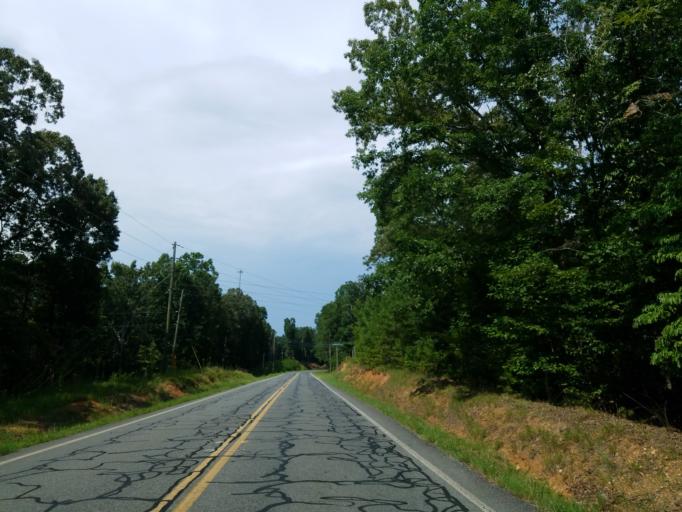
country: US
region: Georgia
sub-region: Gilmer County
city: Ellijay
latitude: 34.5861
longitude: -84.5996
